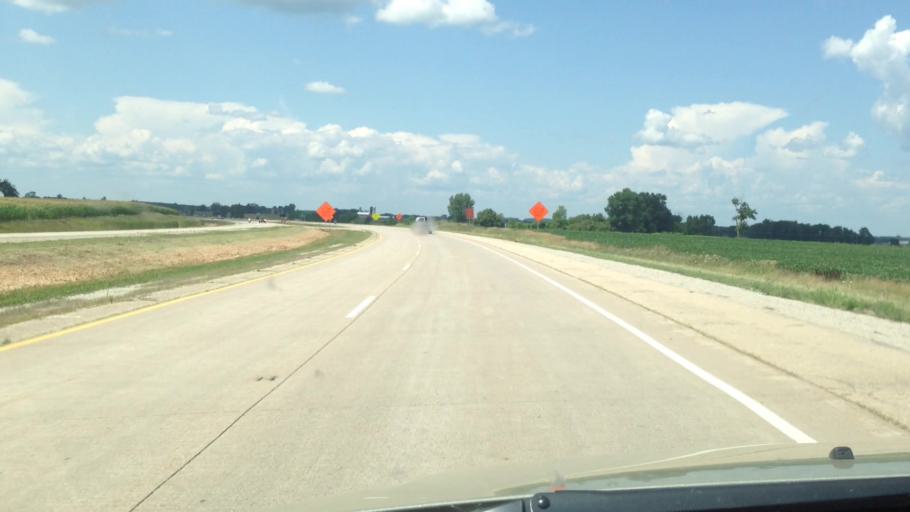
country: US
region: Wisconsin
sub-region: Brown County
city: Pulaski
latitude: 44.6826
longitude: -88.3124
